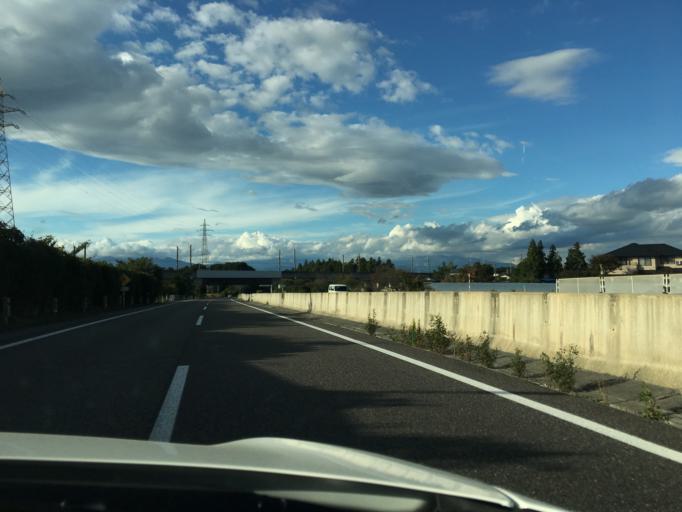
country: JP
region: Fukushima
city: Sukagawa
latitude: 37.3063
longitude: 140.3471
